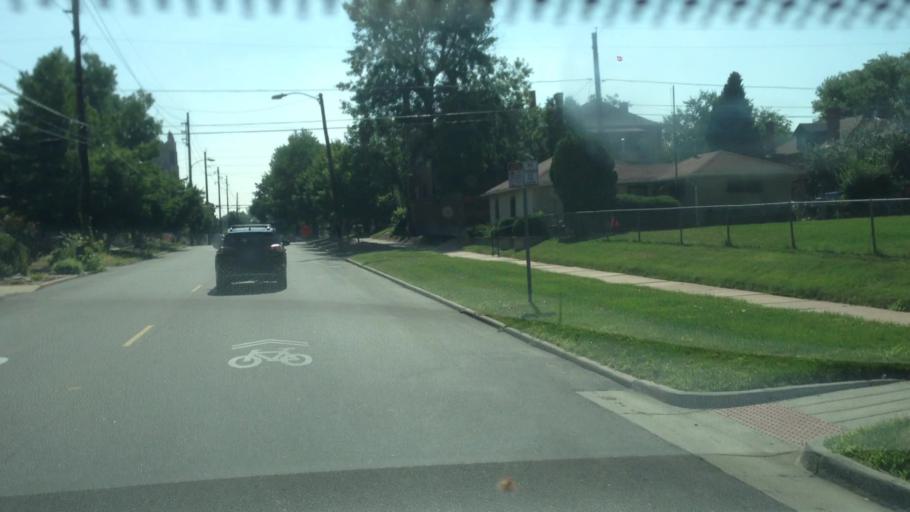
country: US
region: Colorado
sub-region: Denver County
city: Denver
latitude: 39.7507
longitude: -104.9634
